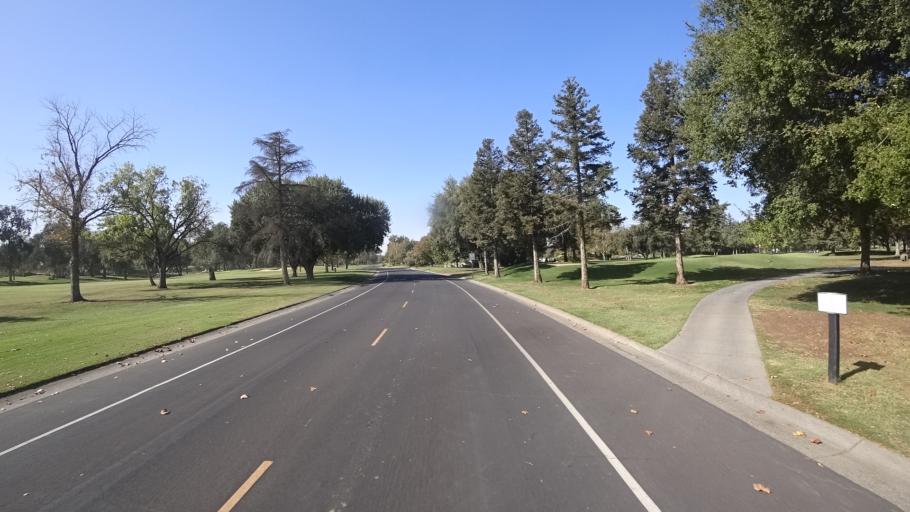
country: US
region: California
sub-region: Yolo County
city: Davis
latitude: 38.5449
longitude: -121.6873
